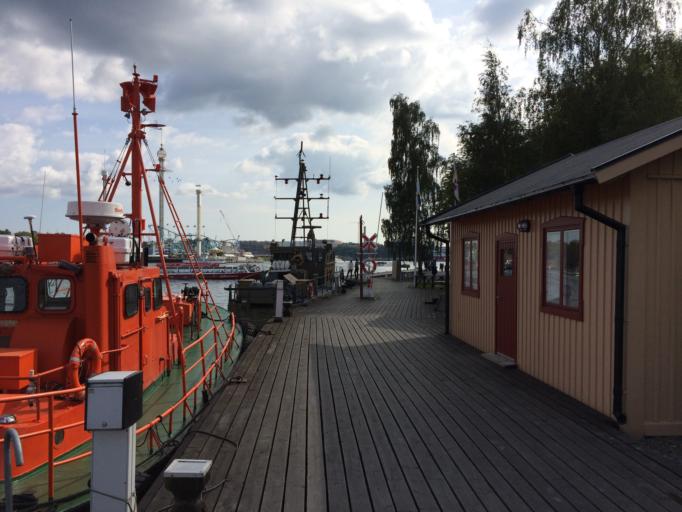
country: SE
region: Stockholm
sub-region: Stockholms Kommun
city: OEstermalm
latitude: 59.3259
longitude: 18.0882
